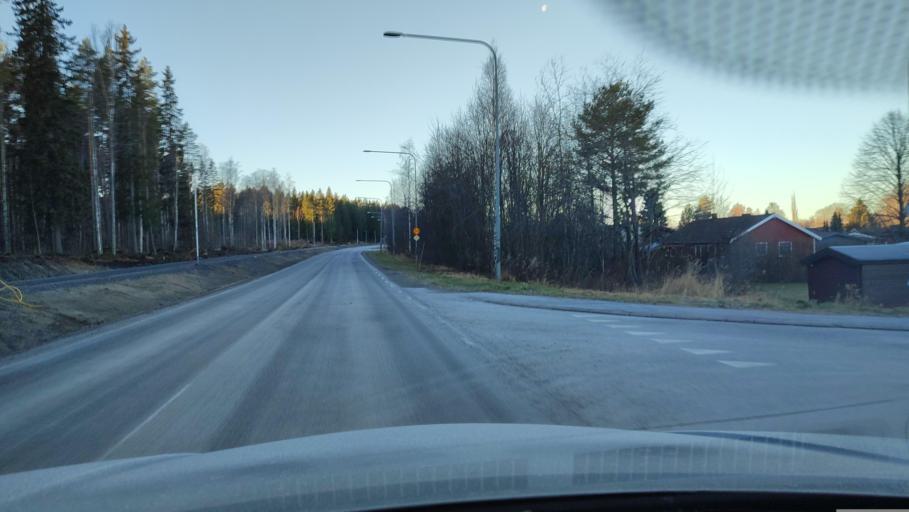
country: SE
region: Vaesterbotten
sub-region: Skelleftea Kommun
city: Viken
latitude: 64.7399
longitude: 20.9307
